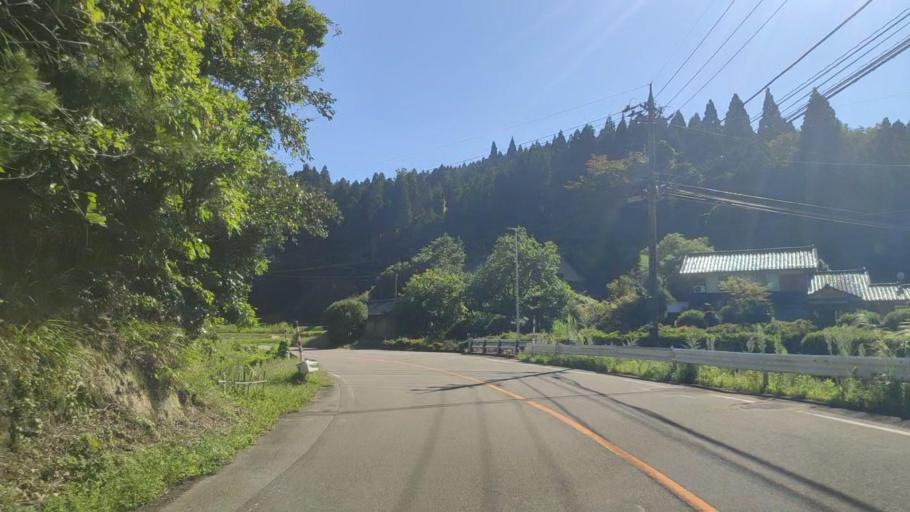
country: JP
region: Ishikawa
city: Nanao
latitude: 37.3336
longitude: 137.2075
